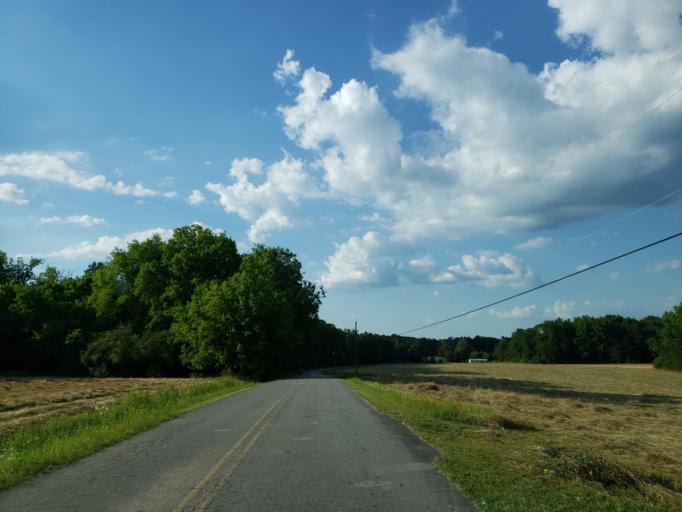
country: US
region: Georgia
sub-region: Haralson County
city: Buchanan
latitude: 33.9088
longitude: -85.2742
